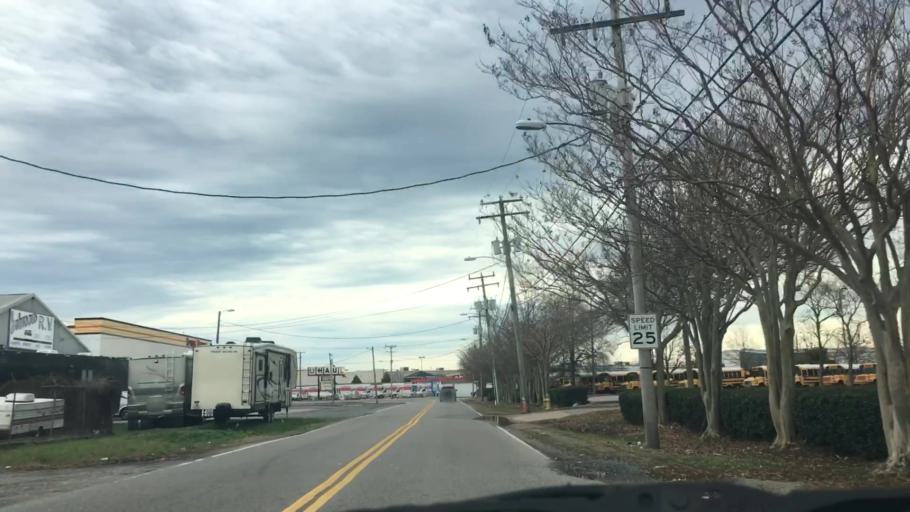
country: US
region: Virginia
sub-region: City of Norfolk
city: Norfolk
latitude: 36.8594
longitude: -76.2163
